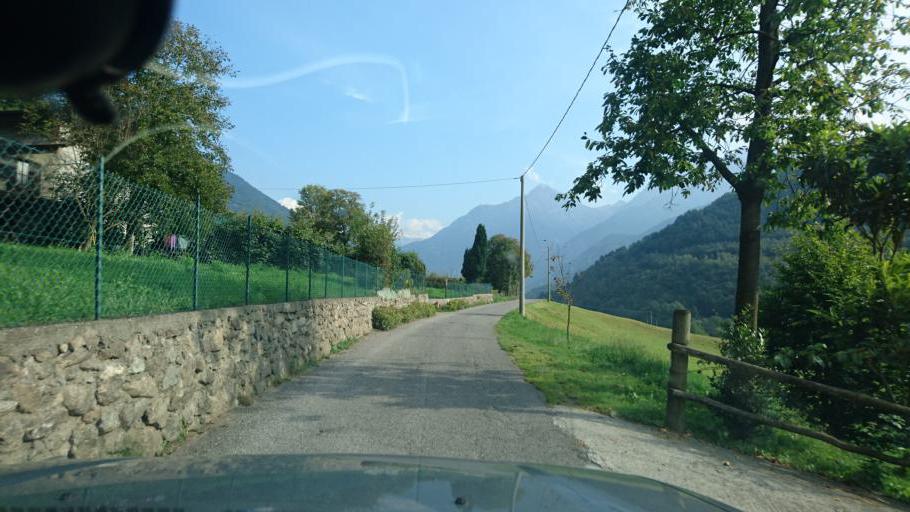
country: IT
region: Lombardy
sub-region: Provincia di Brescia
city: Malonno
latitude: 46.1031
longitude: 10.3075
